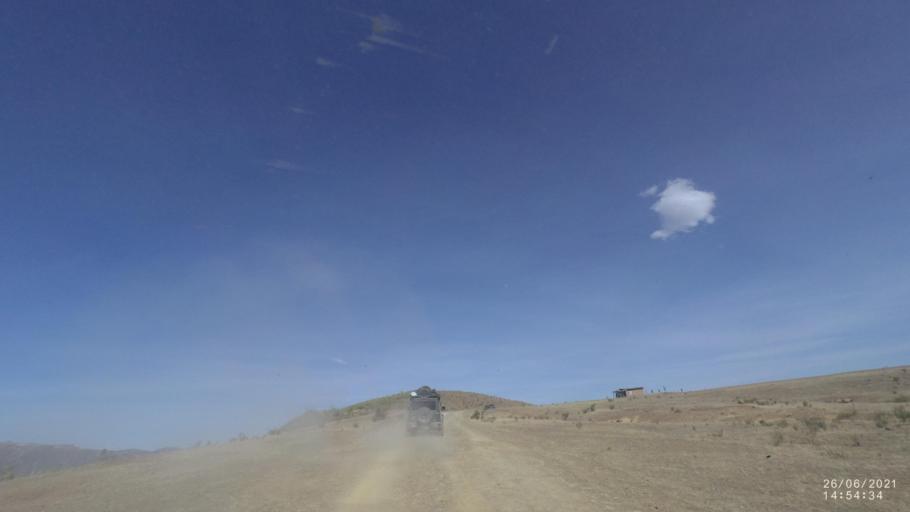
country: BO
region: Cochabamba
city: Mizque
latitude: -17.9322
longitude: -65.6267
